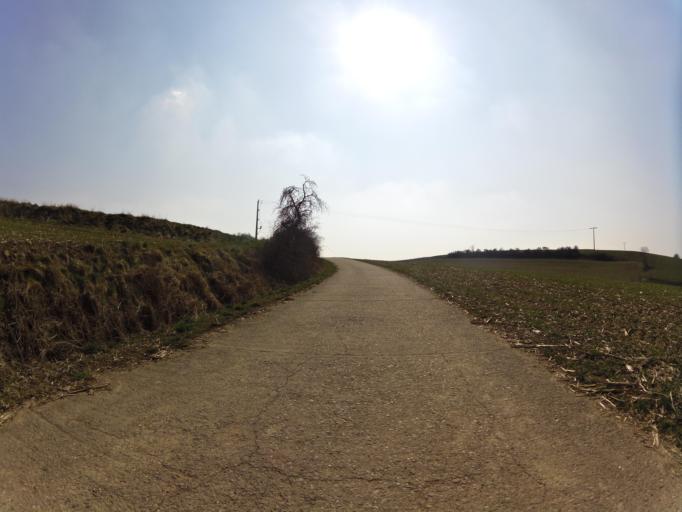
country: DE
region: Bavaria
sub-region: Regierungsbezirk Unterfranken
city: Gaukonigshofen
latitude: 49.6715
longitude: 9.9931
